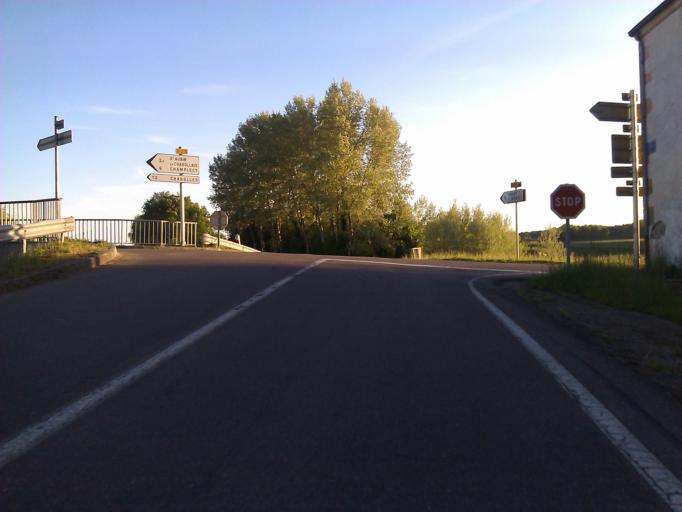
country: FR
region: Bourgogne
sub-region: Departement de Saone-et-Loire
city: Palinges
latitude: 46.5067
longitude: 4.1868
